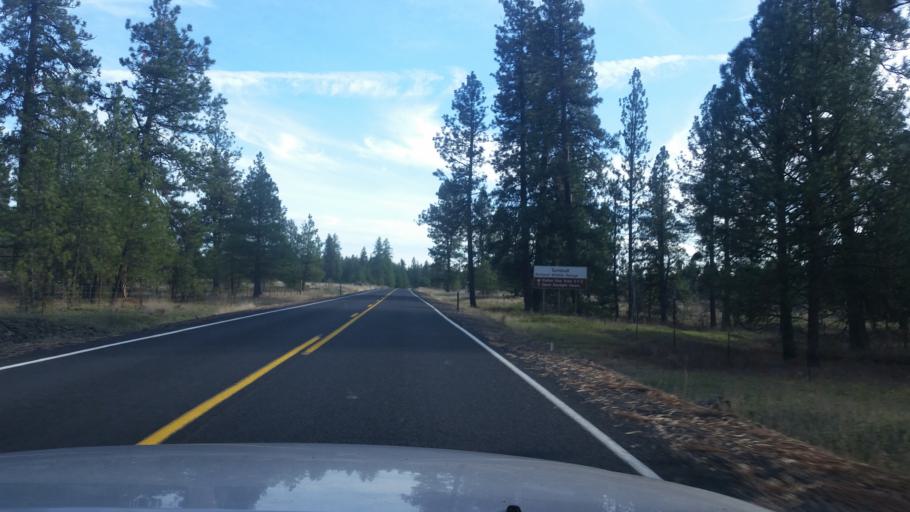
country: US
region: Washington
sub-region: Spokane County
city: Cheney
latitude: 47.4560
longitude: -117.5783
